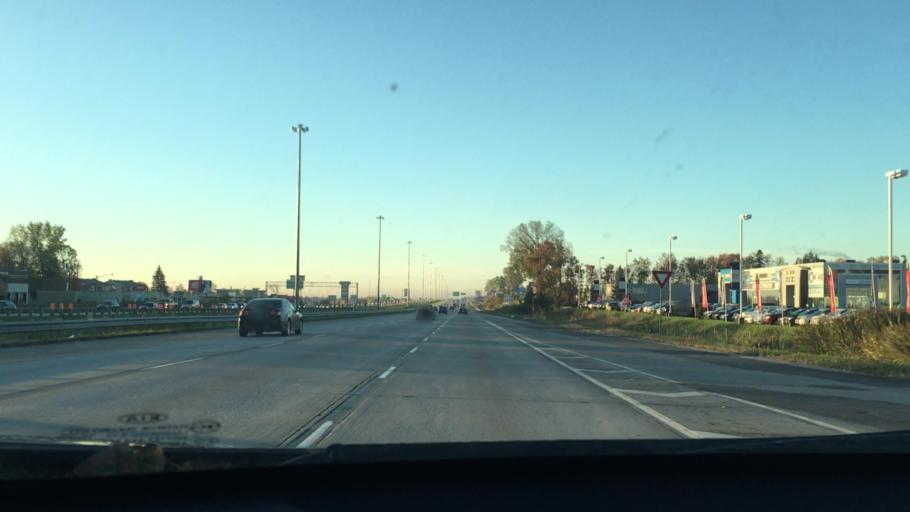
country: CA
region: Quebec
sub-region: Laurentides
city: Saint-Jerome
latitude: 45.7745
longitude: -74.0209
